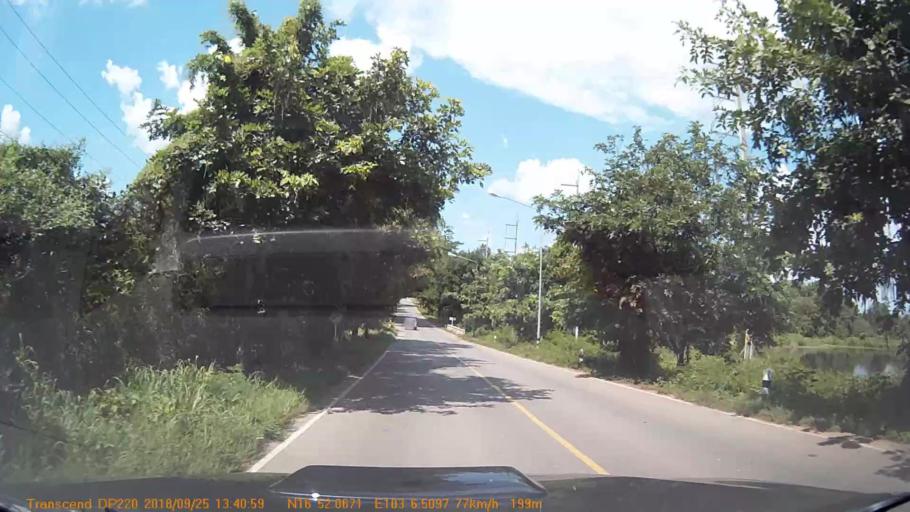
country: TH
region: Changwat Udon Thani
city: Si That
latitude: 16.8679
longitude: 103.1085
